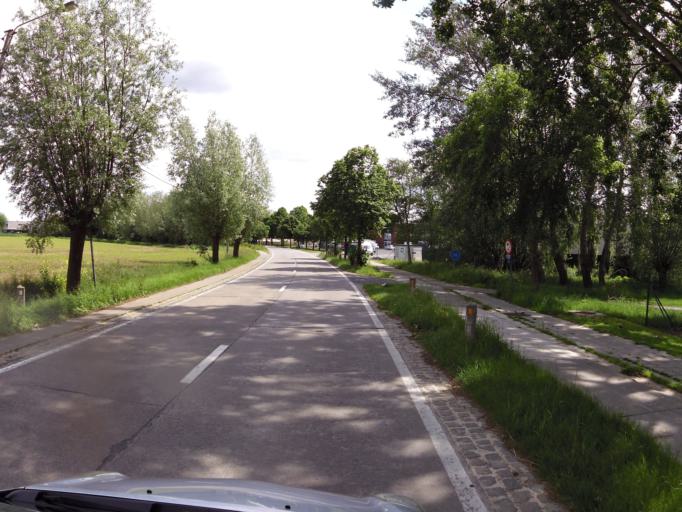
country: BE
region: Flanders
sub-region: Provincie West-Vlaanderen
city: Ieper
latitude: 50.8613
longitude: 2.9075
